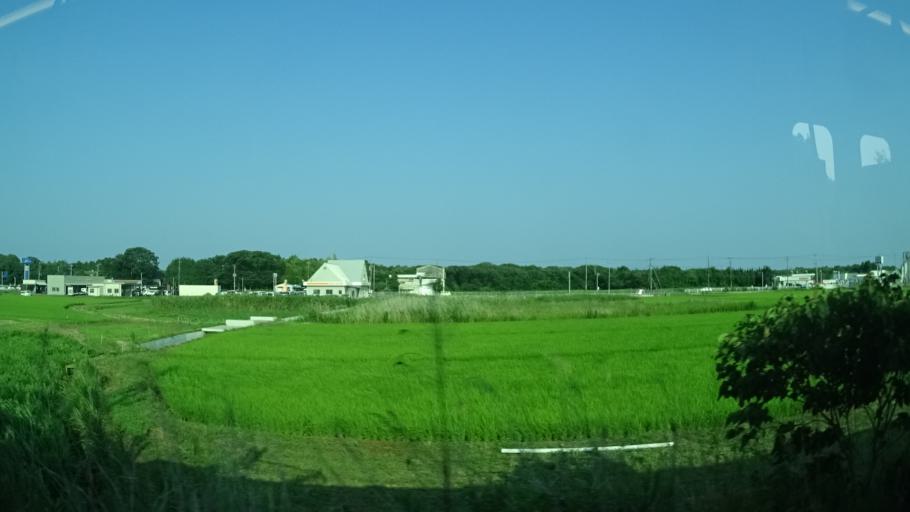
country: JP
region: Ibaraki
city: Takahagi
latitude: 36.7502
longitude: 140.7279
